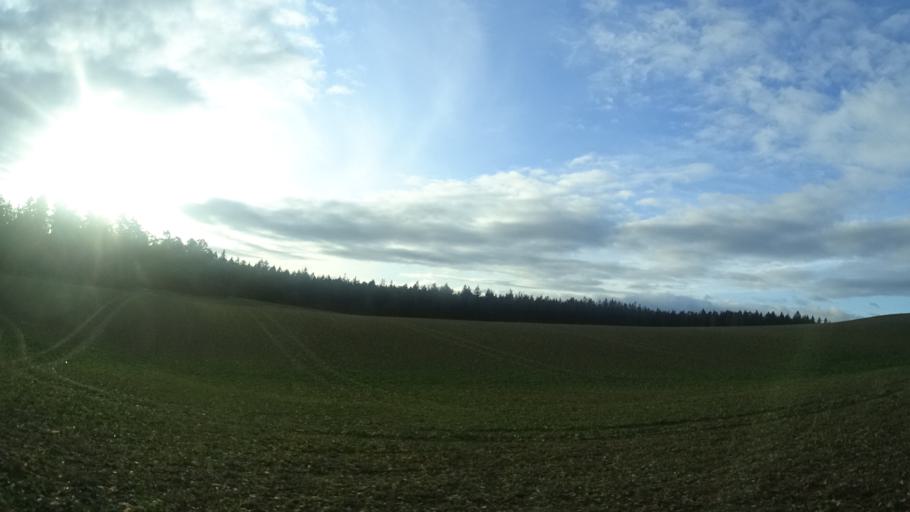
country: DE
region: Thuringia
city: Rottenbach
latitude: 50.7321
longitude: 11.1911
